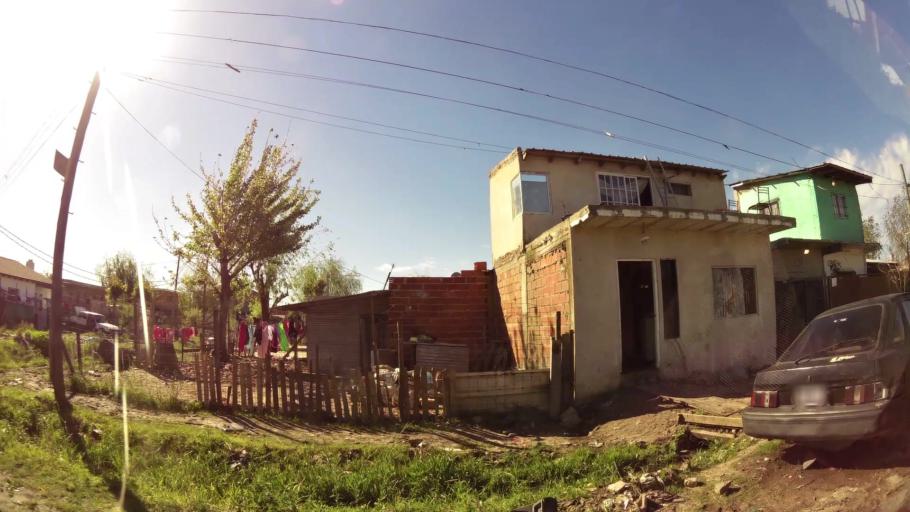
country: AR
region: Buenos Aires
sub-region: Partido de Quilmes
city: Quilmes
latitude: -34.7604
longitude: -58.3163
